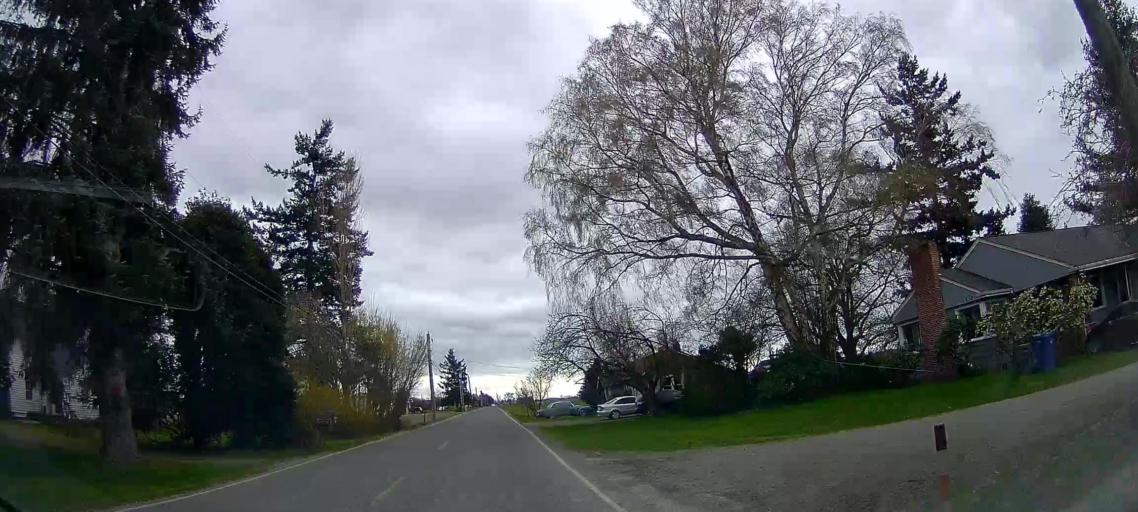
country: US
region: Washington
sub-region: Skagit County
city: Mount Vernon
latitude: 48.4034
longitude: -122.4008
